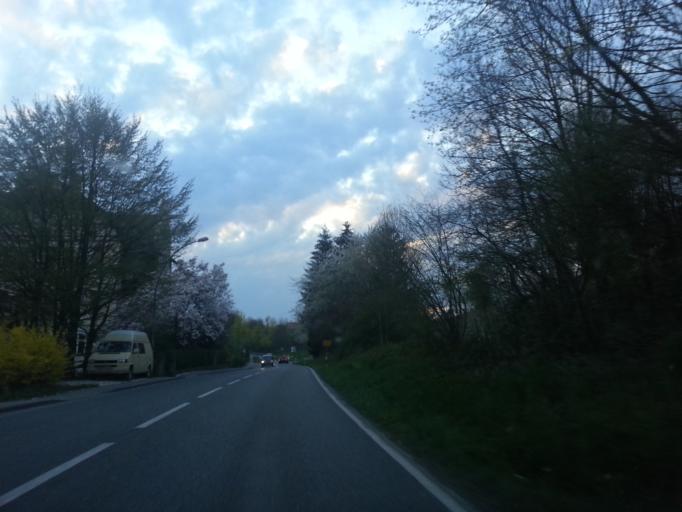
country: DE
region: Bavaria
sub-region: Swabia
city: Bodolz
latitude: 47.5637
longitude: 9.6730
